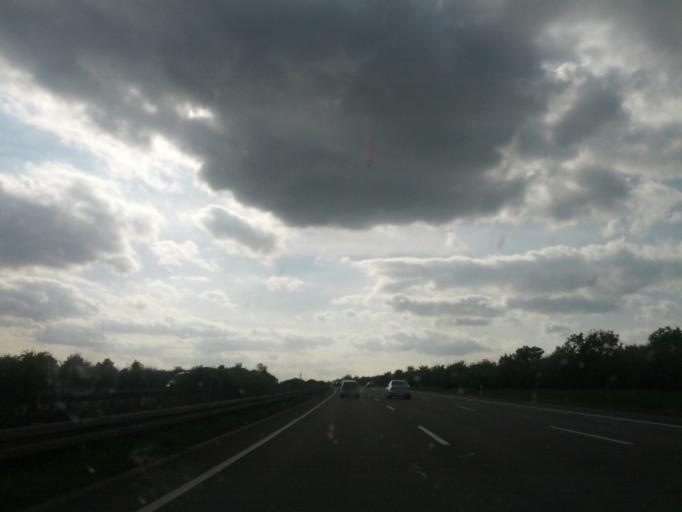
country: DE
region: Thuringia
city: Vollersroda
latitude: 50.9426
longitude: 11.3232
